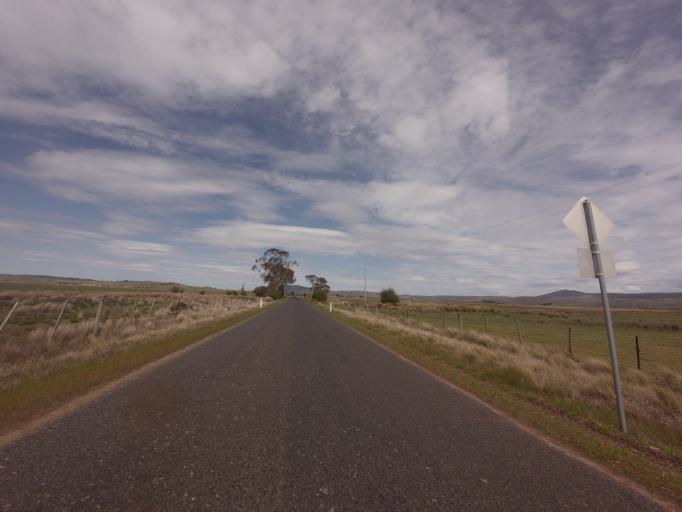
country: AU
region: Tasmania
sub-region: Northern Midlands
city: Evandale
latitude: -41.8660
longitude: 147.3494
